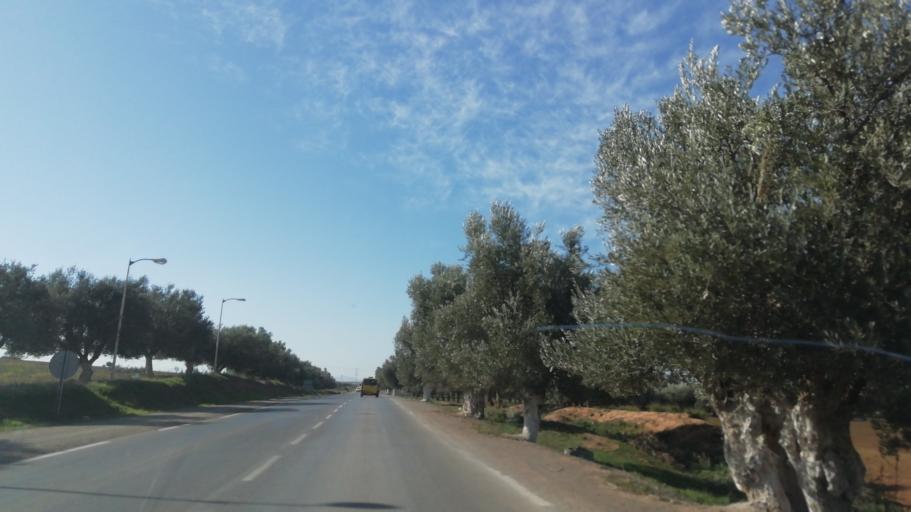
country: DZ
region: Tlemcen
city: Ouled Mimoun
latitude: 35.0237
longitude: -0.8965
